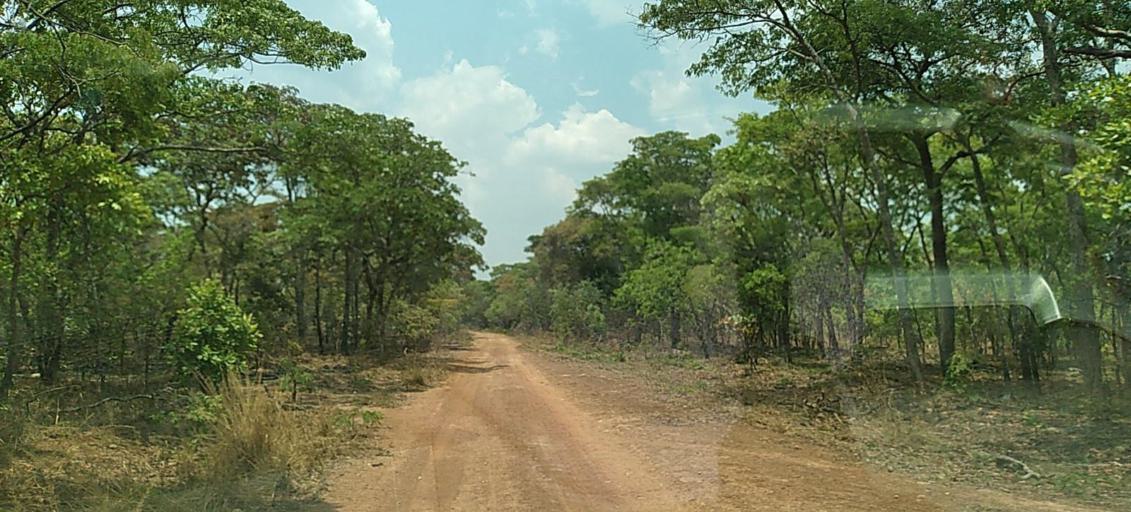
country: ZM
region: Copperbelt
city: Chingola
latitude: -12.7789
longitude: 27.6727
